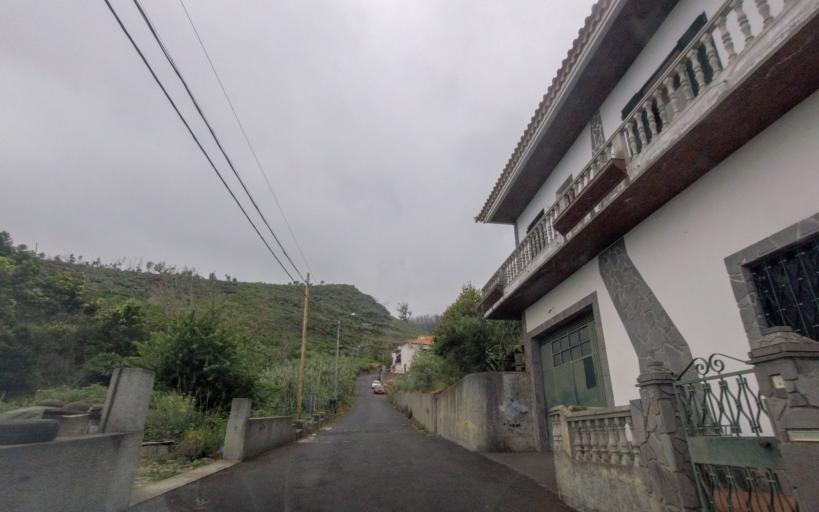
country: PT
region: Madeira
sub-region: Funchal
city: Nossa Senhora do Monte
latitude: 32.6771
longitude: -16.9138
